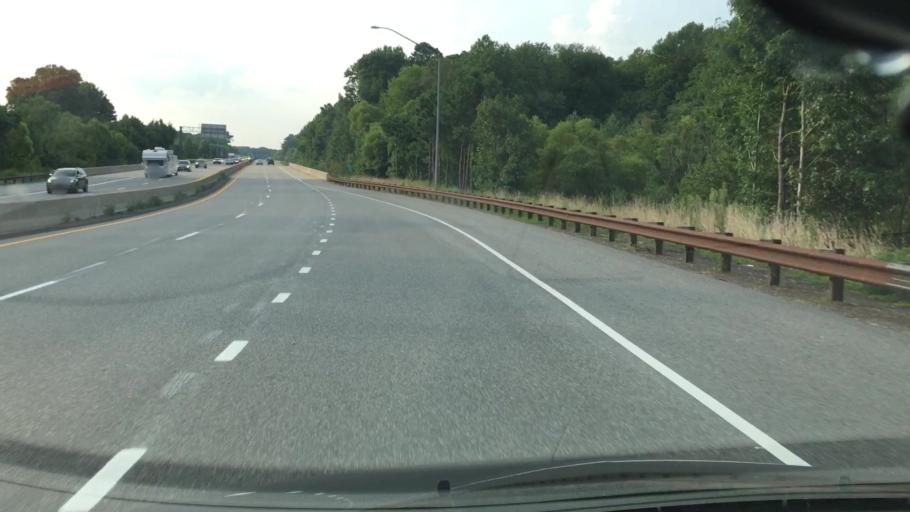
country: US
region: Maryland
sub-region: Worcester County
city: Ocean Pines
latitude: 38.3939
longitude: -75.2041
